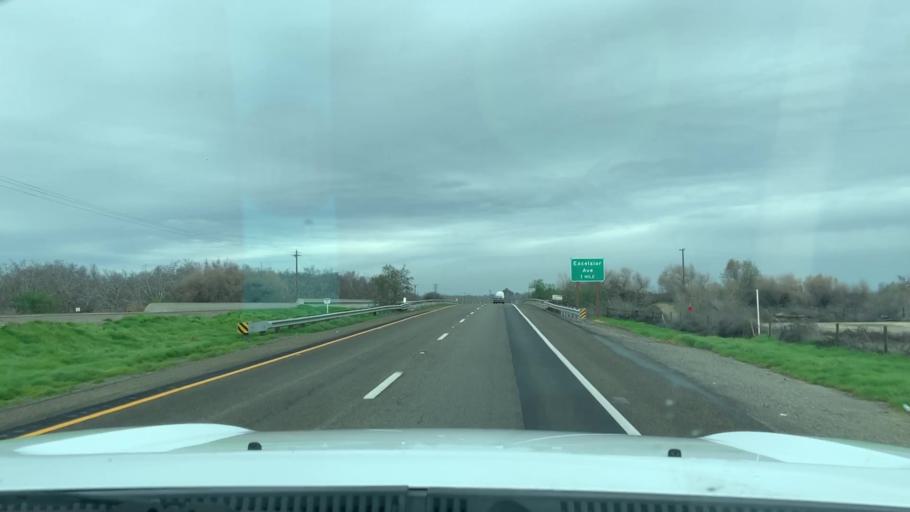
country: US
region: California
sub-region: Fresno County
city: Riverdale
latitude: 36.3854
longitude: -119.8095
